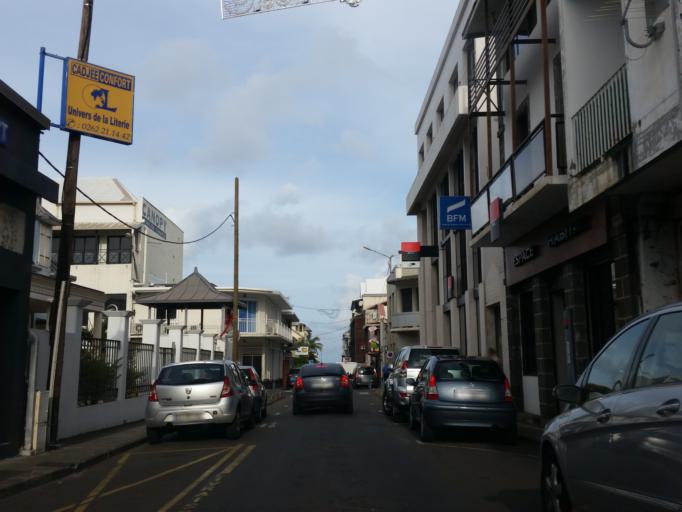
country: RE
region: Reunion
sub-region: Reunion
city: Saint-Denis
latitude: -20.8766
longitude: 55.4517
